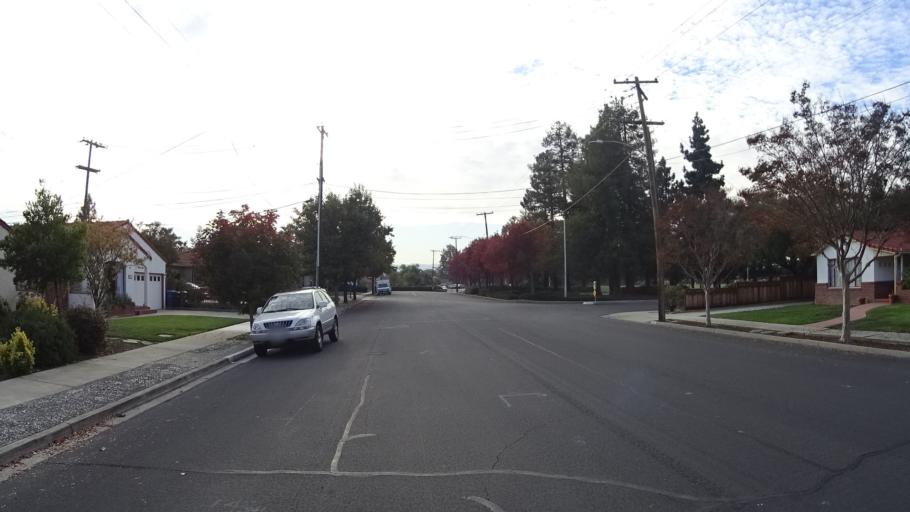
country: US
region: California
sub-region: Santa Clara County
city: Santa Clara
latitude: 37.3444
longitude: -121.9531
